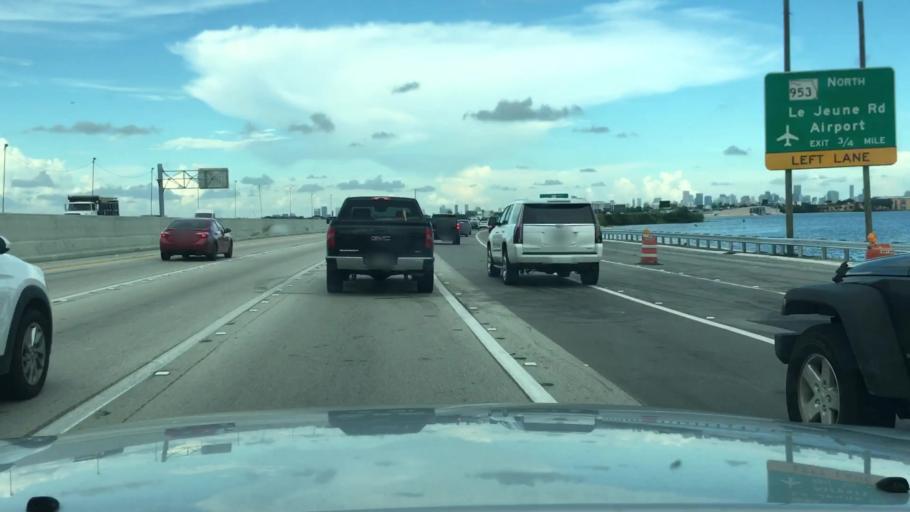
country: US
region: Florida
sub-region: Miami-Dade County
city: West Miami
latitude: 25.7848
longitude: -80.2827
